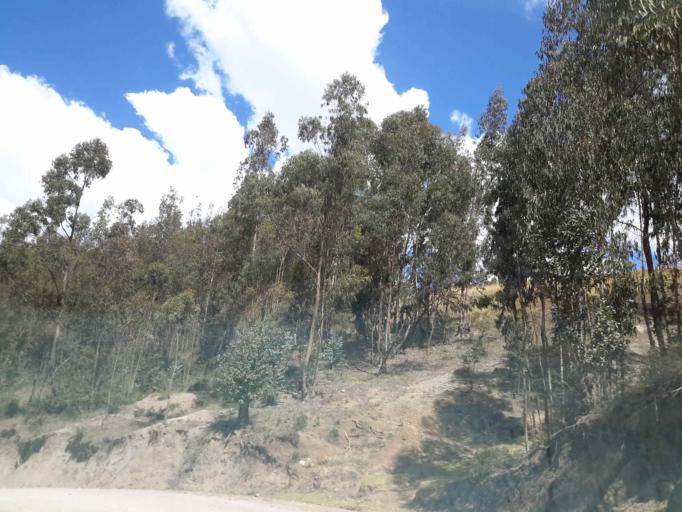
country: PE
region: Apurimac
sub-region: Provincia de Andahuaylas
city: Pacucha
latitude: -13.6222
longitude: -73.3351
